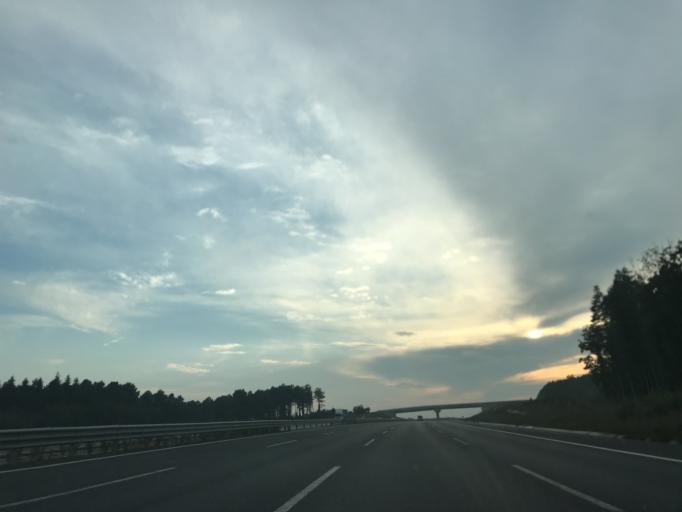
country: TR
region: Istanbul
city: Sancaktepe
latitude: 41.0437
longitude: 29.2207
